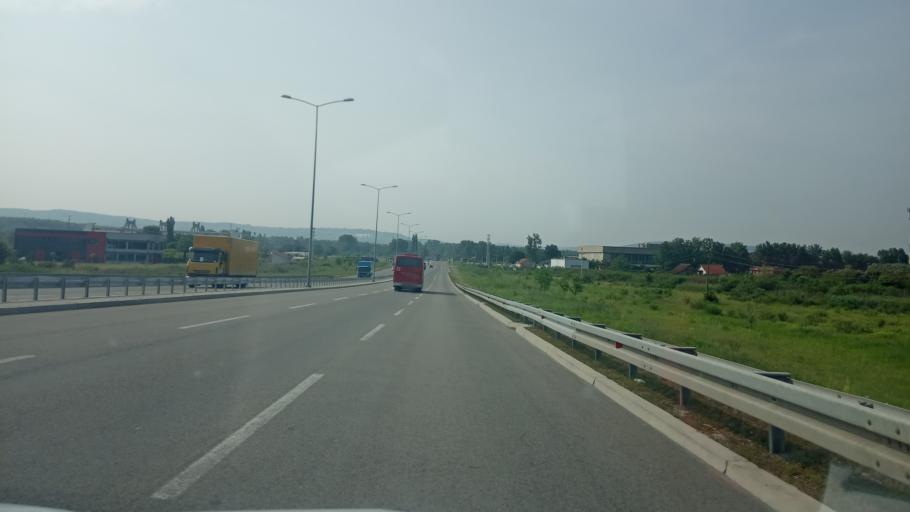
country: RS
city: Ovca
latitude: 44.8544
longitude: 20.5157
